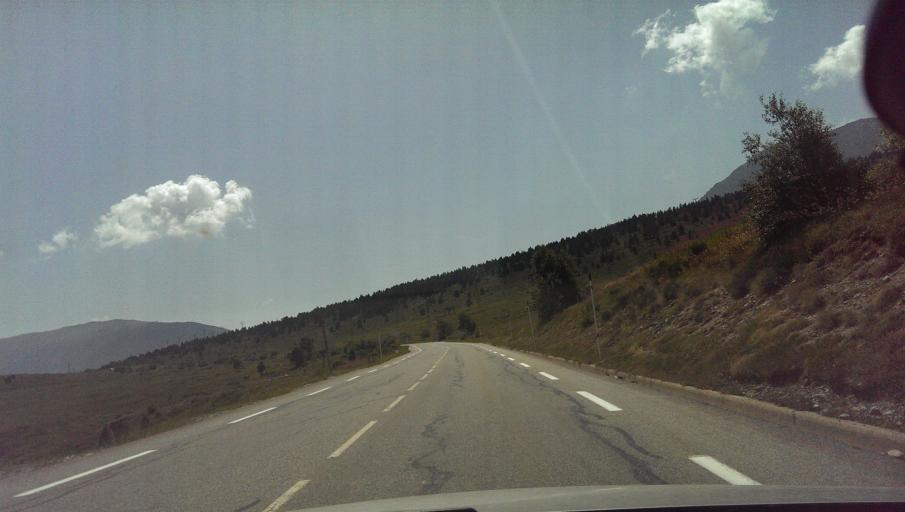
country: AD
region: Encamp
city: Pas de la Casa
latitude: 42.5663
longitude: 1.8000
